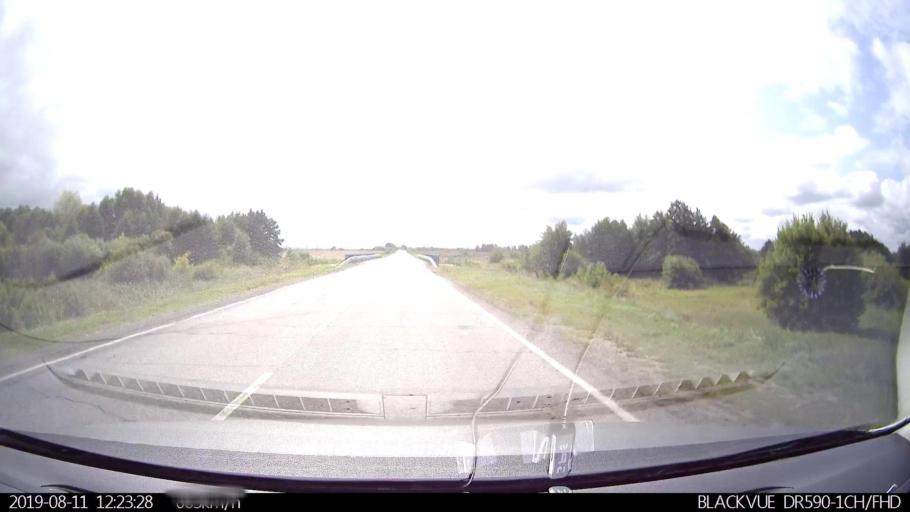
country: RU
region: Ulyanovsk
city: Ignatovka
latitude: 53.8948
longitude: 47.9504
